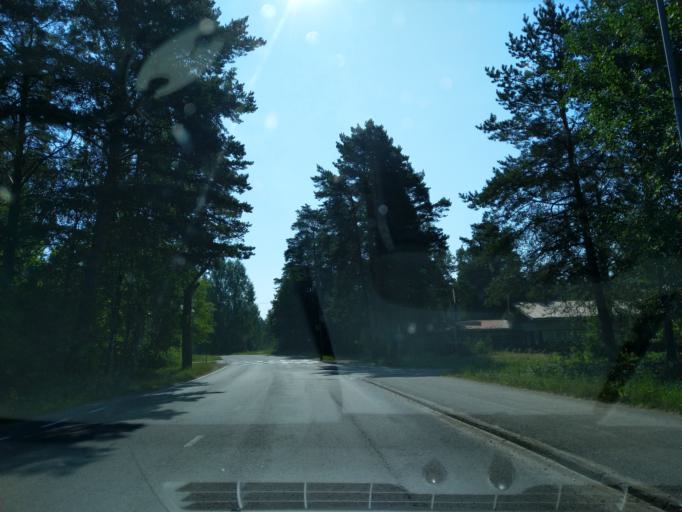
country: FI
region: Satakunta
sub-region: Pori
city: Noormarkku
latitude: 61.5880
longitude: 21.8907
